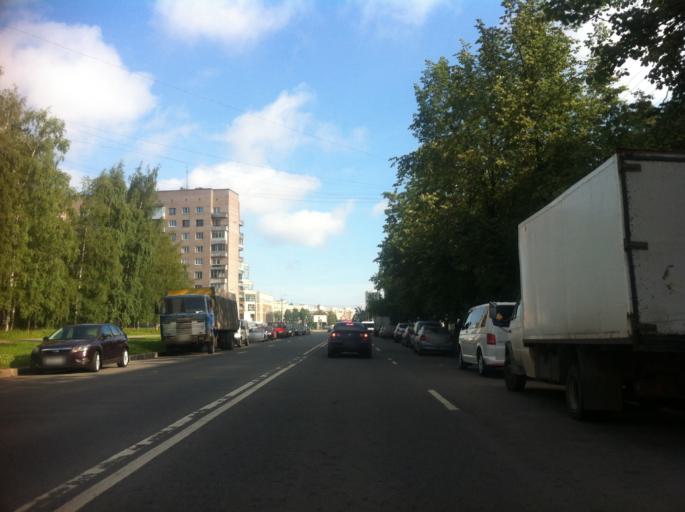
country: RU
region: St.-Petersburg
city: Dachnoye
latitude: 59.8320
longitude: 30.2192
